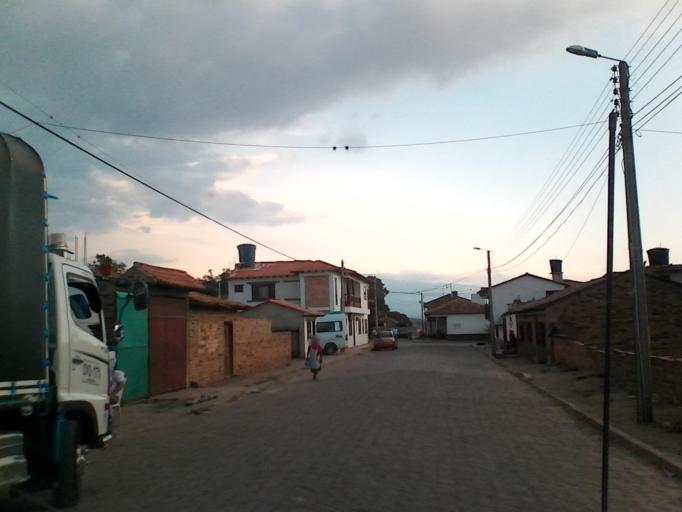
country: CO
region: Boyaca
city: Sachica
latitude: 5.5834
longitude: -73.5410
